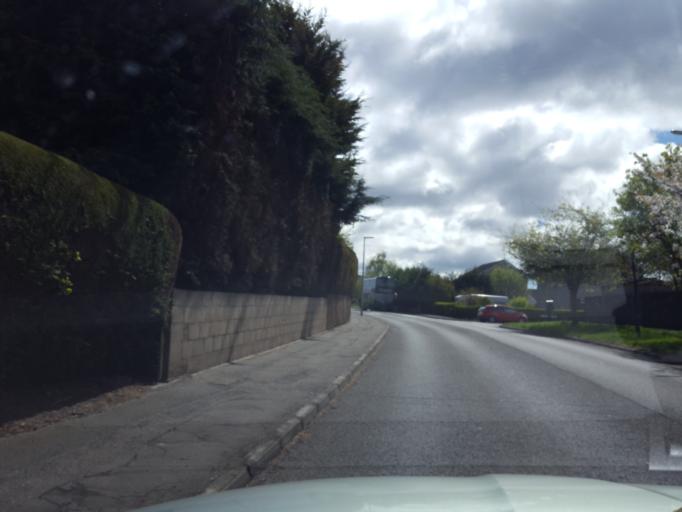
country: GB
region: Scotland
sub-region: Angus
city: Muirhead
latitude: 56.4702
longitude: -3.0538
